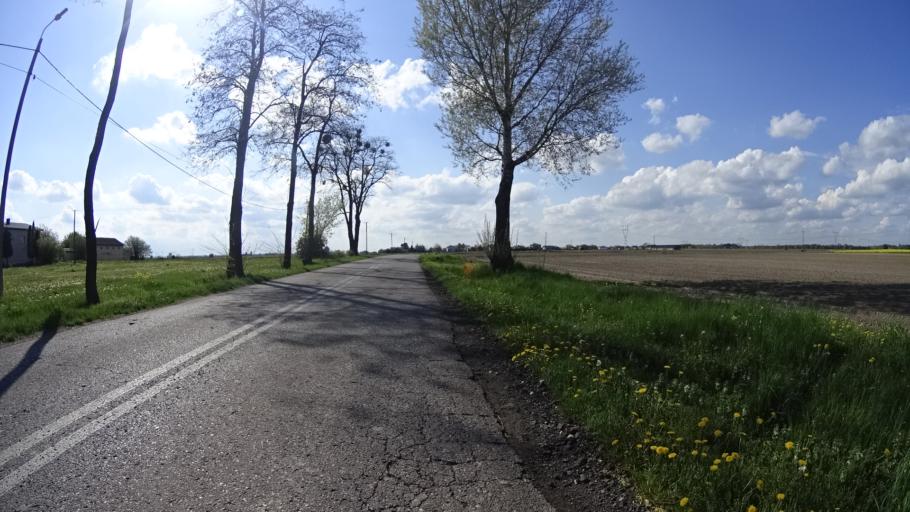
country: PL
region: Masovian Voivodeship
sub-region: Powiat warszawski zachodni
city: Jozefow
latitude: 52.2329
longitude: 20.6851
